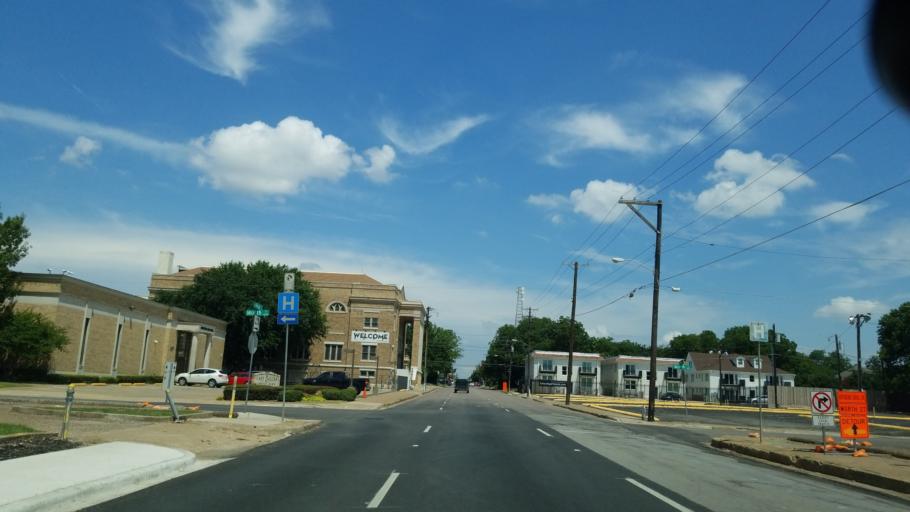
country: US
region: Texas
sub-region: Dallas County
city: Dallas
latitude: 32.7933
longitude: -96.7729
